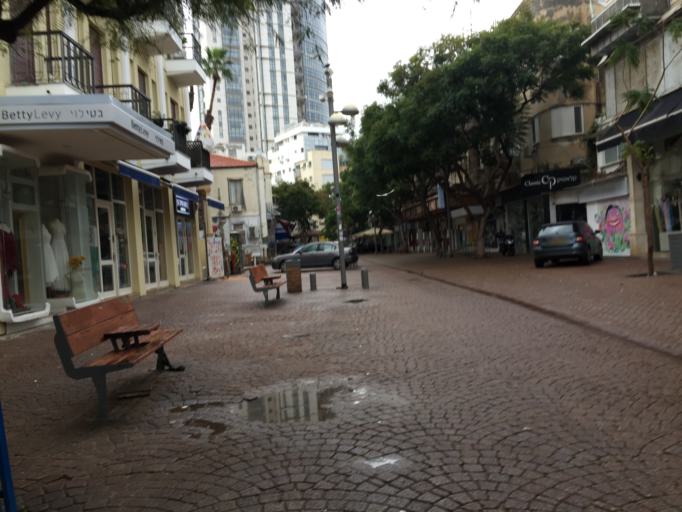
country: IL
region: Tel Aviv
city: Tel Aviv
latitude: 32.0677
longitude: 34.7702
